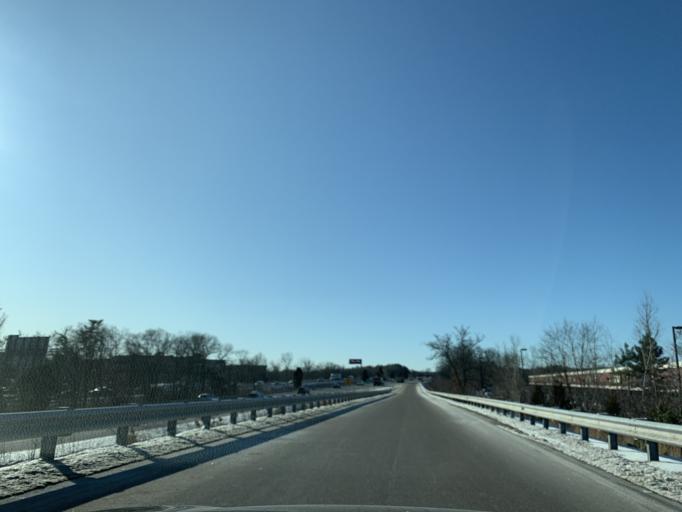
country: US
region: Massachusetts
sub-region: Norfolk County
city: Canton
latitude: 42.1929
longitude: -71.1519
